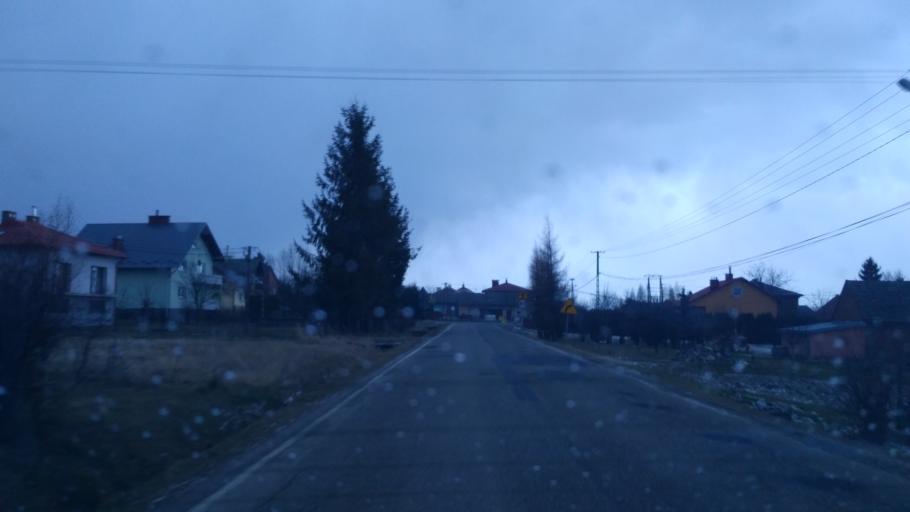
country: PL
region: Subcarpathian Voivodeship
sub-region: Powiat rzeszowski
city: Hyzne
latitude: 49.9244
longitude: 22.1955
